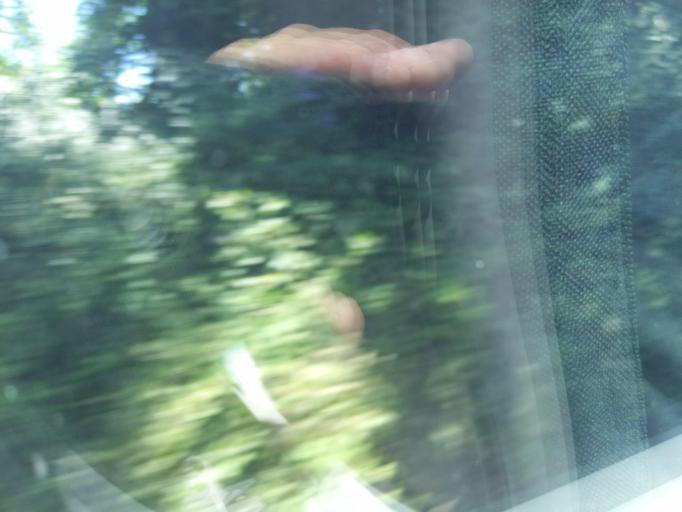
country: GB
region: England
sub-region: Cornwall
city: St Austell
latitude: 50.3415
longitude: -4.7959
